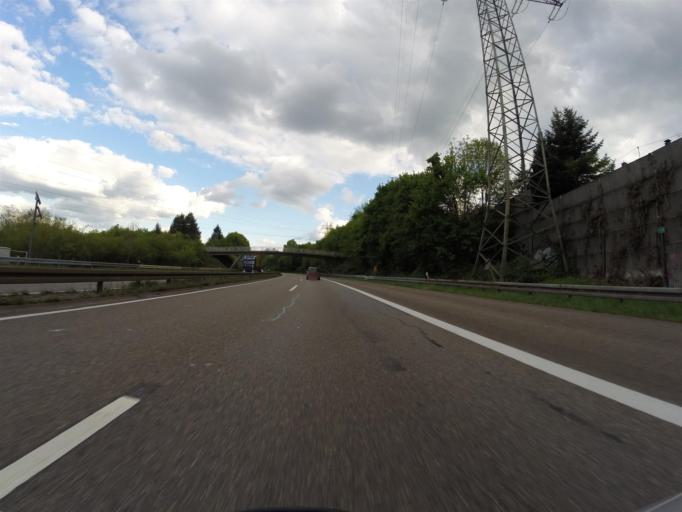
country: DE
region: Saarland
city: Volklingen
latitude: 49.2451
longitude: 6.8346
